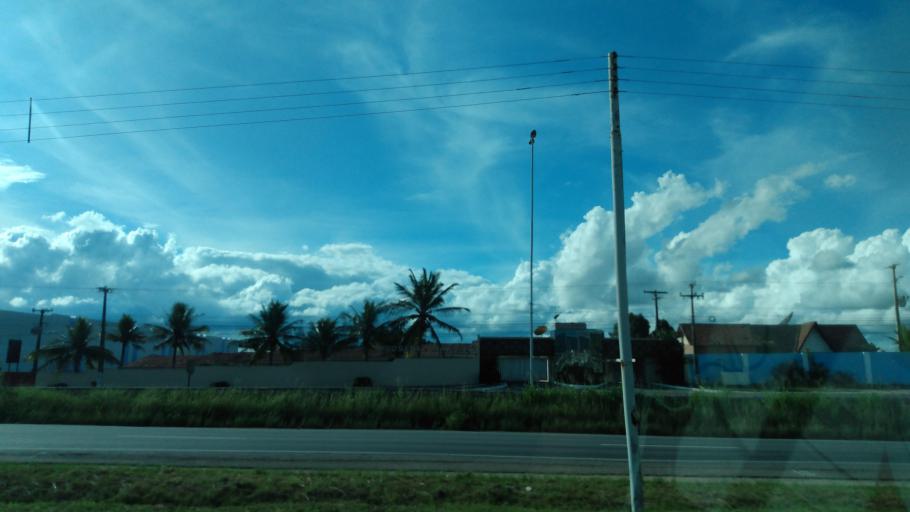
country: ET
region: Oromiya
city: Gore
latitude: 8.1979
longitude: 35.5830
